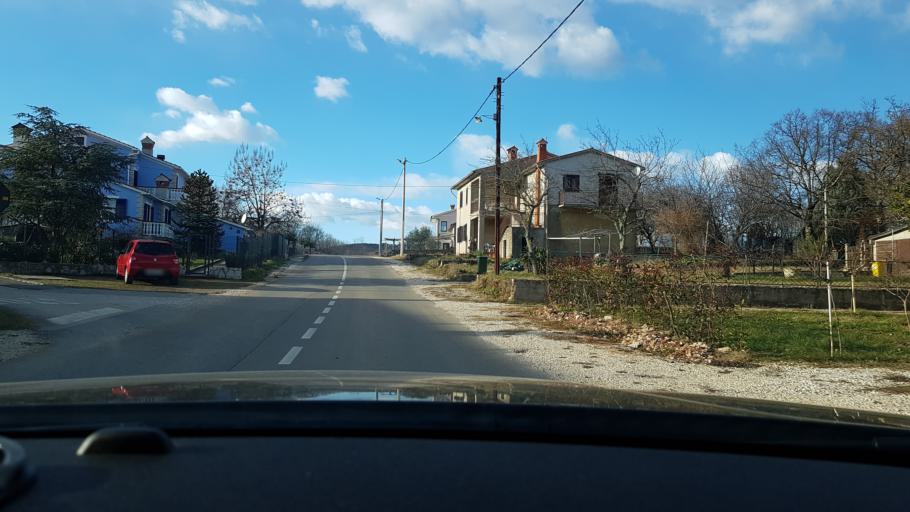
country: HR
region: Istarska
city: Vinez
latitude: 45.1040
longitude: 14.0989
